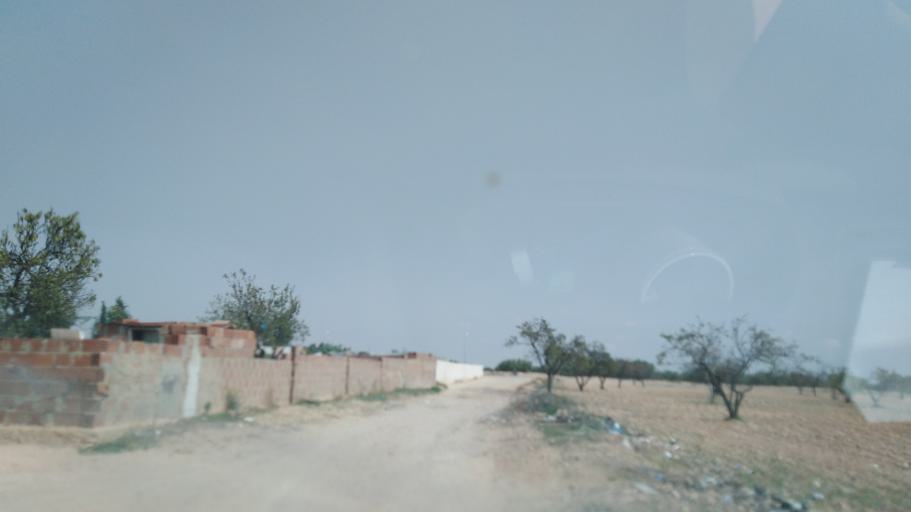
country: TN
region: Safaqis
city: Sfax
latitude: 34.6614
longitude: 10.5769
